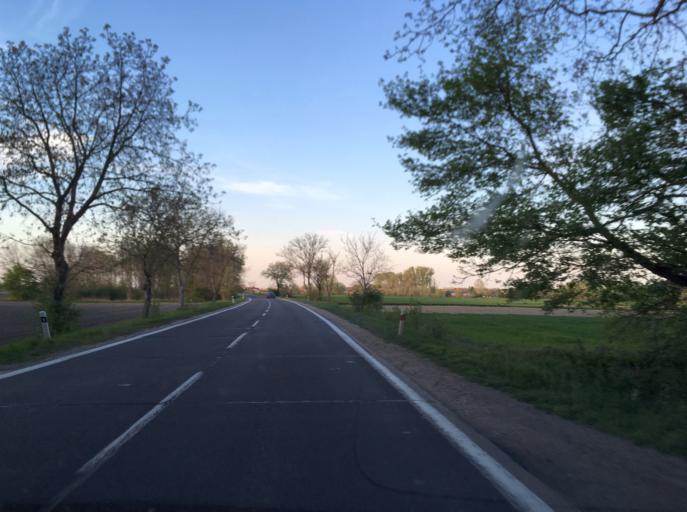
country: SK
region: Trnavsky
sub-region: Okres Dunajska Streda
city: Velky Meder
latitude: 47.8433
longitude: 17.7290
